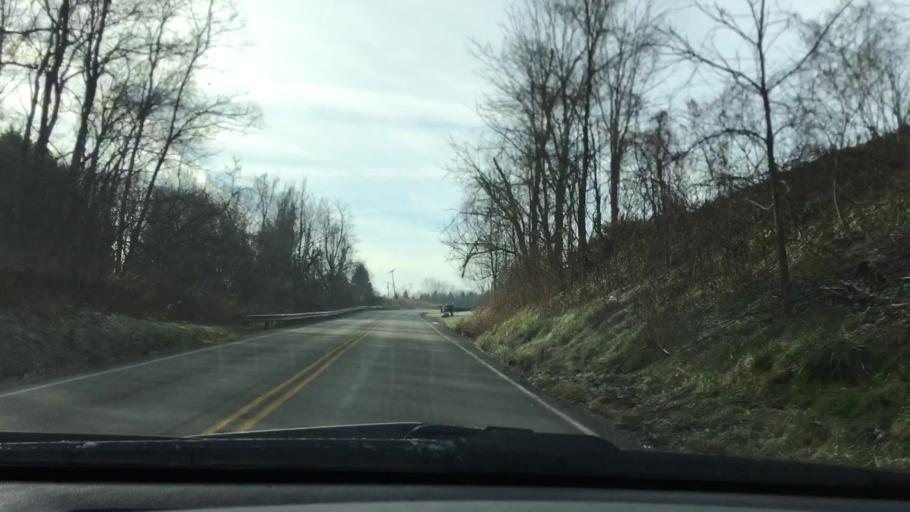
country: US
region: Pennsylvania
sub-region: Allegheny County
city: Industry
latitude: 40.2602
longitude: -79.7686
